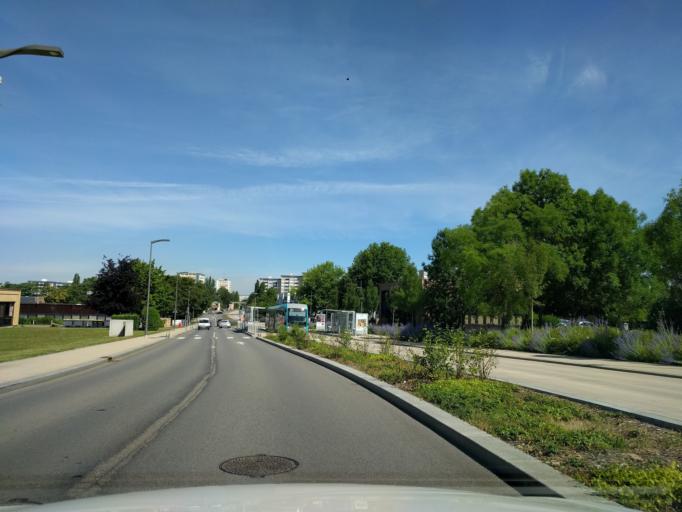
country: FR
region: Lorraine
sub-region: Departement de la Moselle
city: Peltre
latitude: 49.1046
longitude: 6.2237
